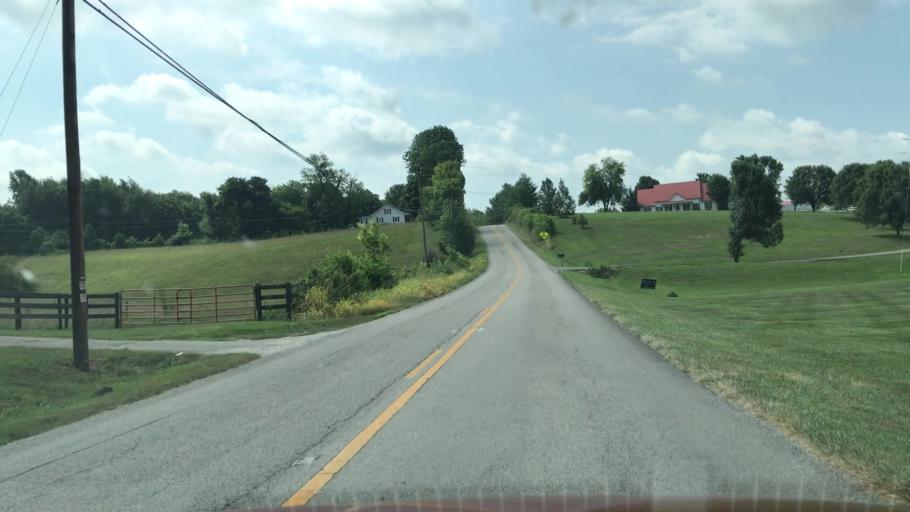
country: US
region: Kentucky
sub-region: Barren County
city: Glasgow
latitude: 36.9673
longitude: -85.8920
